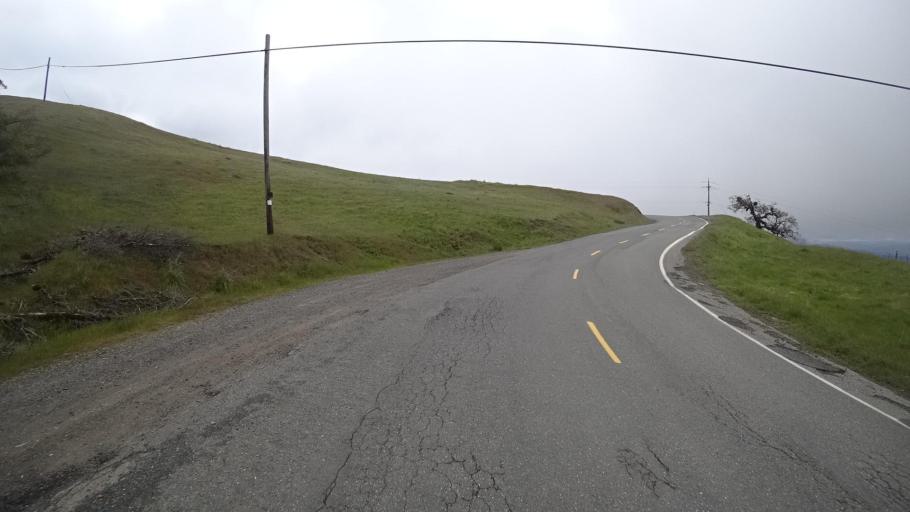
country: US
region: California
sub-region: Humboldt County
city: Redway
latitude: 40.1040
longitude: -123.6919
